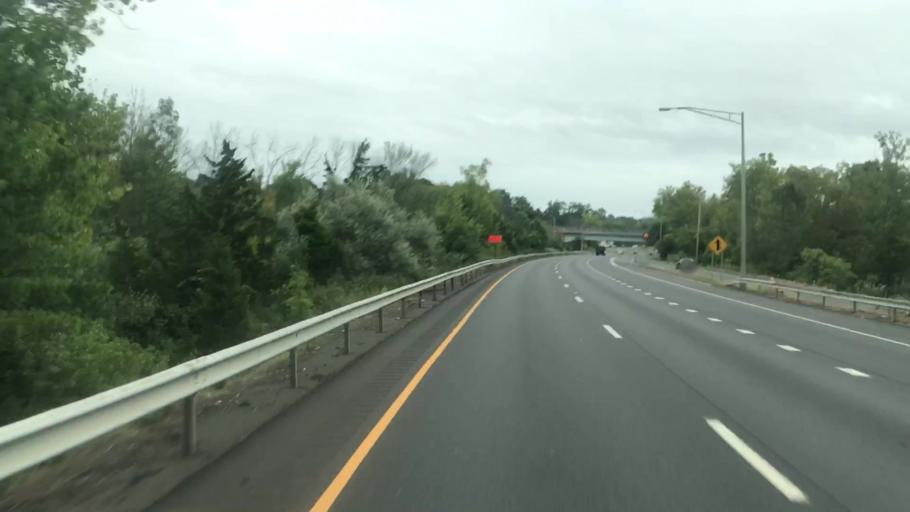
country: US
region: Connecticut
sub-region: Hartford County
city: Farmington
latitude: 41.7196
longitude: -72.7936
